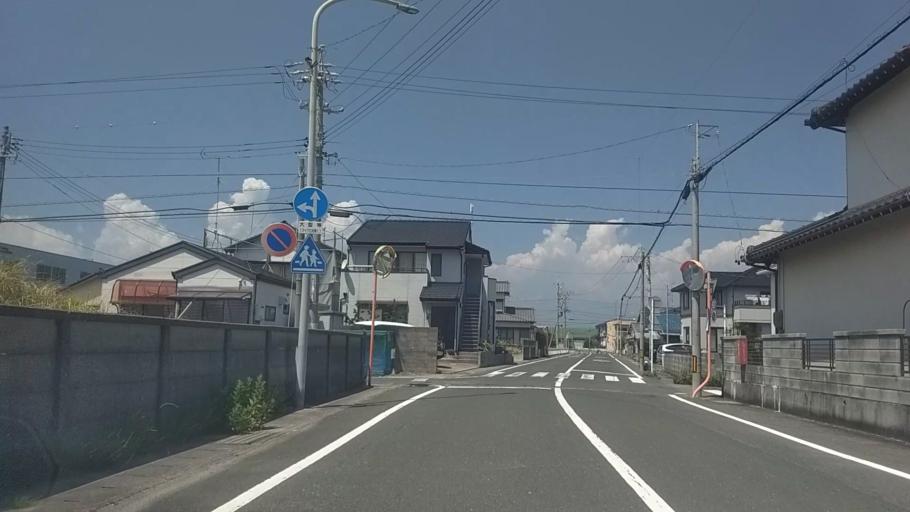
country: JP
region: Shizuoka
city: Kosai-shi
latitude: 34.6834
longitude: 137.5777
